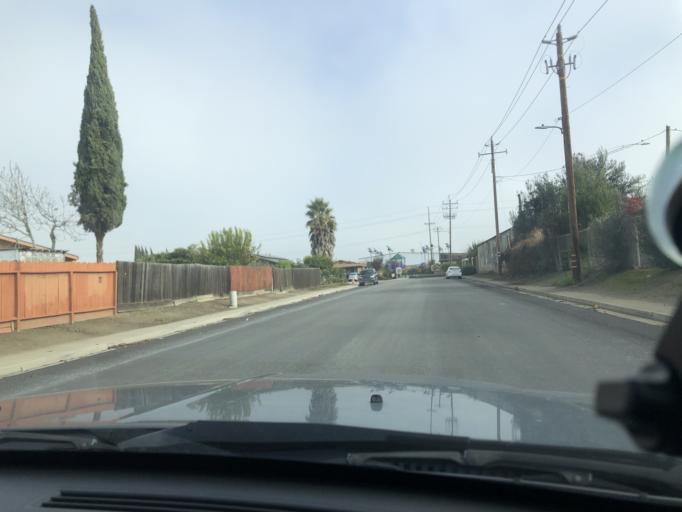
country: US
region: California
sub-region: Monterey County
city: King City
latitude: 36.2190
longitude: -121.1284
